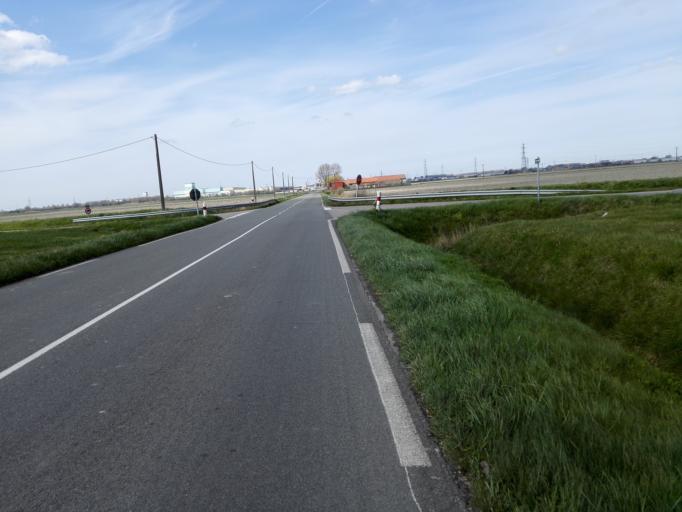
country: FR
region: Nord-Pas-de-Calais
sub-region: Departement du Nord
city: Spycker
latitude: 50.9731
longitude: 2.3134
